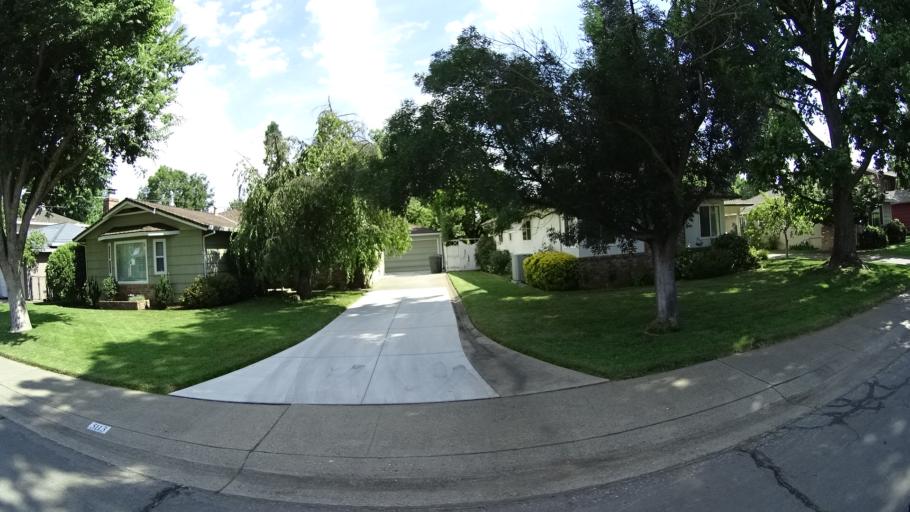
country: US
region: California
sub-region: Sacramento County
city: Sacramento
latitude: 38.5808
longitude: -121.4385
